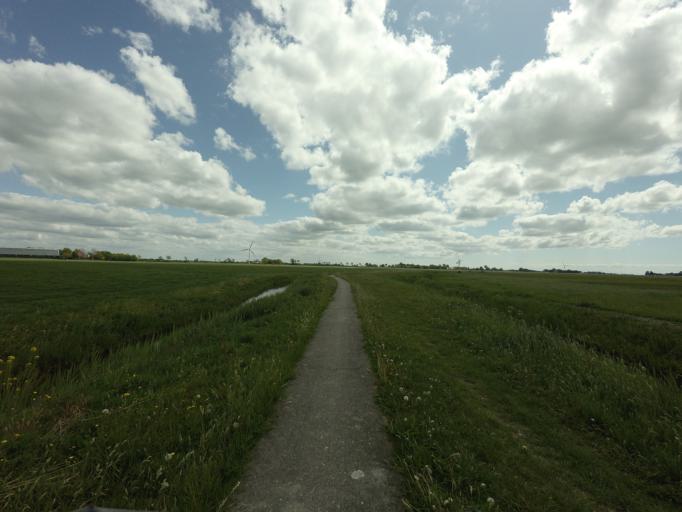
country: NL
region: Friesland
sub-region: Gemeente Littenseradiel
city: Wommels
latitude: 53.1326
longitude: 5.5735
